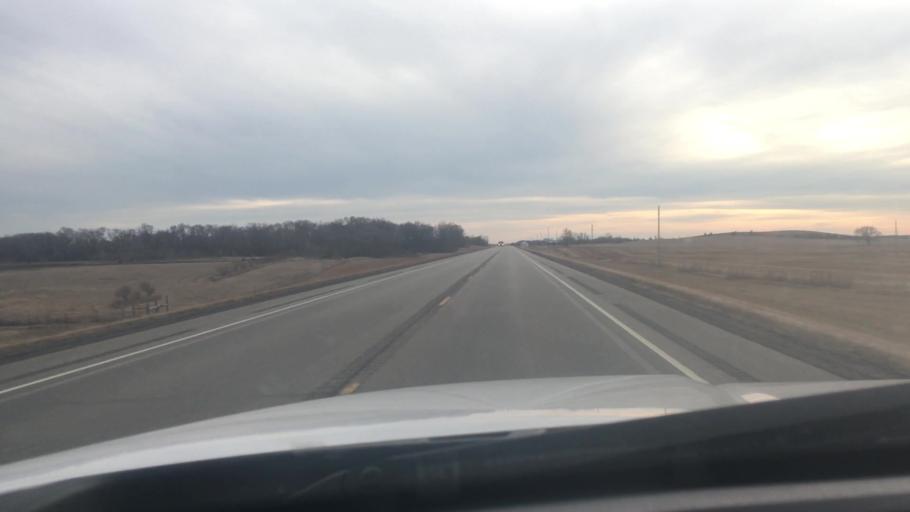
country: US
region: Minnesota
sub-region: Otter Tail County
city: Perham
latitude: 46.3337
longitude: -95.7185
